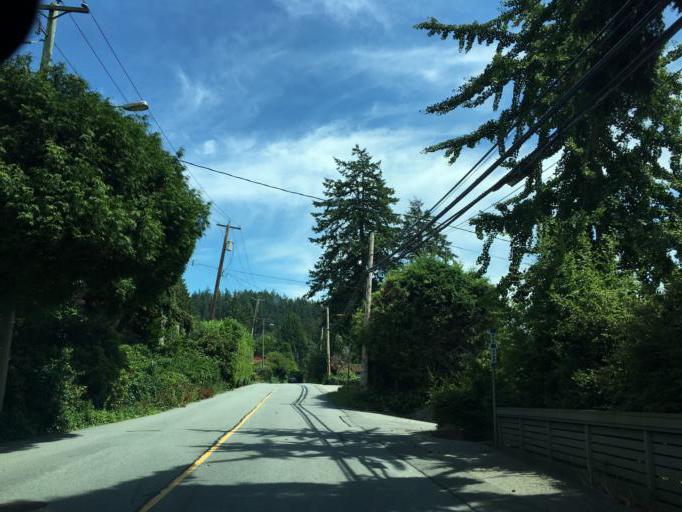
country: CA
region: British Columbia
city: West Vancouver
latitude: 49.3418
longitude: -123.2306
